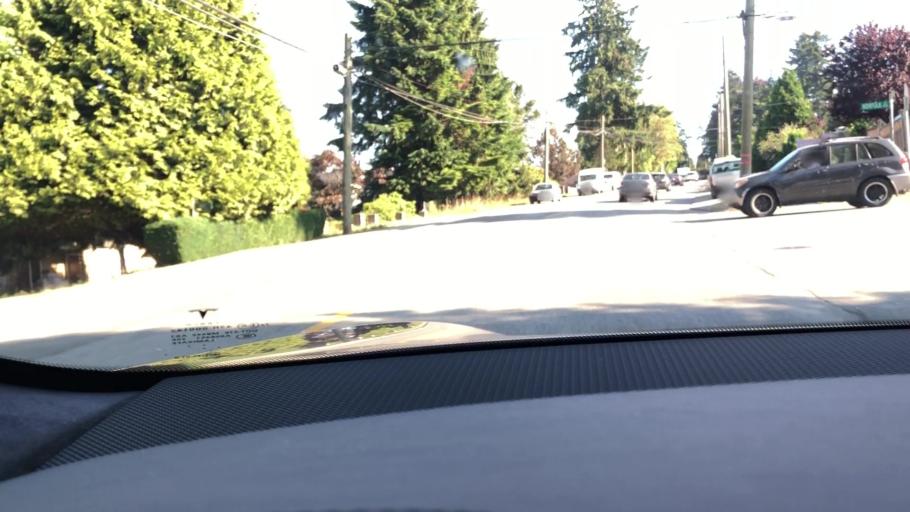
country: CA
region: British Columbia
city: Burnaby
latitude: 49.2552
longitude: -122.9821
